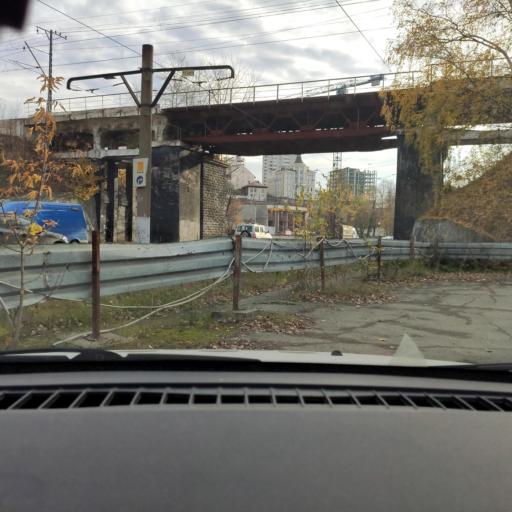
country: RU
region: Perm
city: Perm
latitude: 58.0086
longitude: 56.1926
